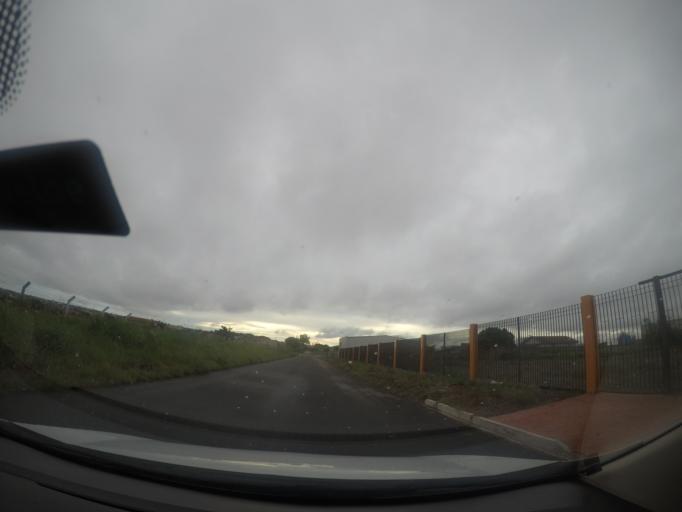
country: BR
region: Goias
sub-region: Goiania
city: Goiania
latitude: -16.7514
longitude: -49.3205
